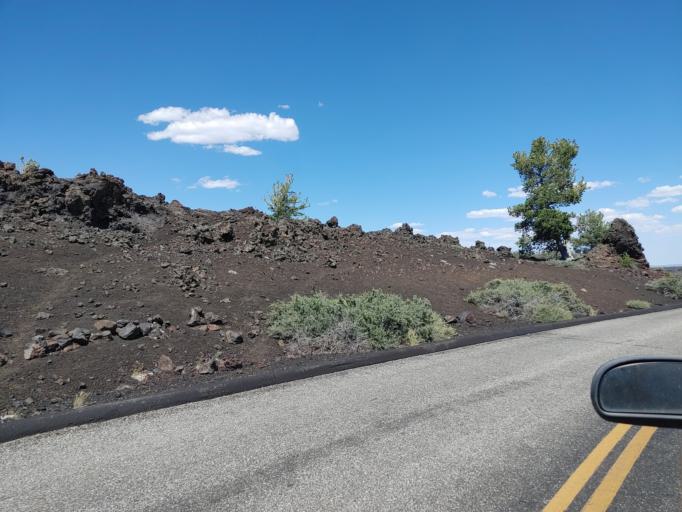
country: US
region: Idaho
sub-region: Butte County
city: Arco
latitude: 43.4578
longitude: -113.5580
